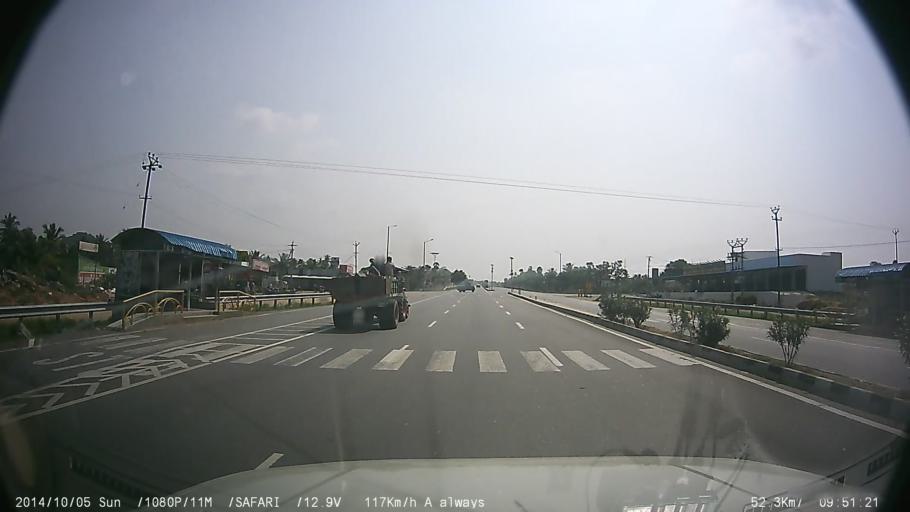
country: IN
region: Tamil Nadu
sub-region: Salem
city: Idappadi
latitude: 11.4936
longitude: 77.8662
